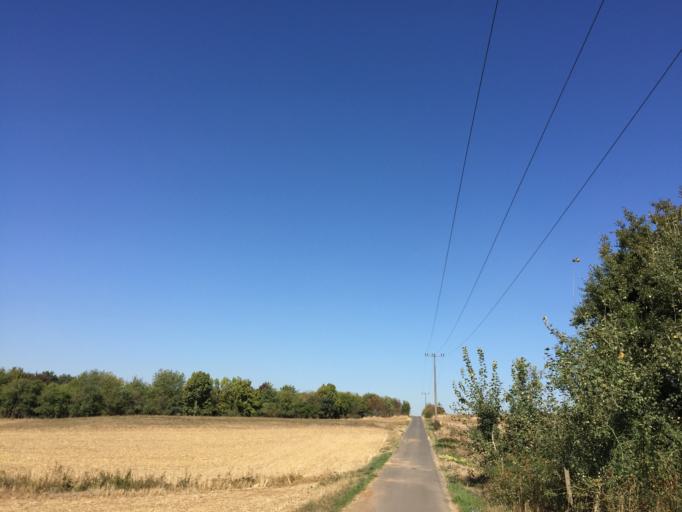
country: DE
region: Hesse
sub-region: Regierungsbezirk Giessen
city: Hungen
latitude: 50.4341
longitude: 8.9309
